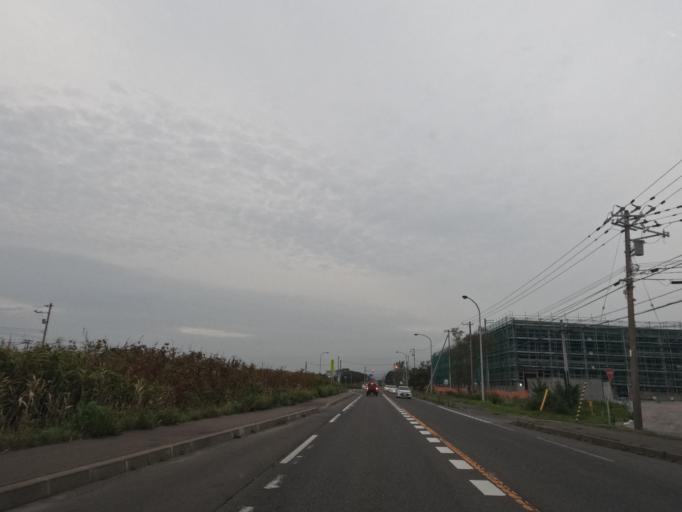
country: JP
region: Hokkaido
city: Date
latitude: 42.3954
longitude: 140.9076
